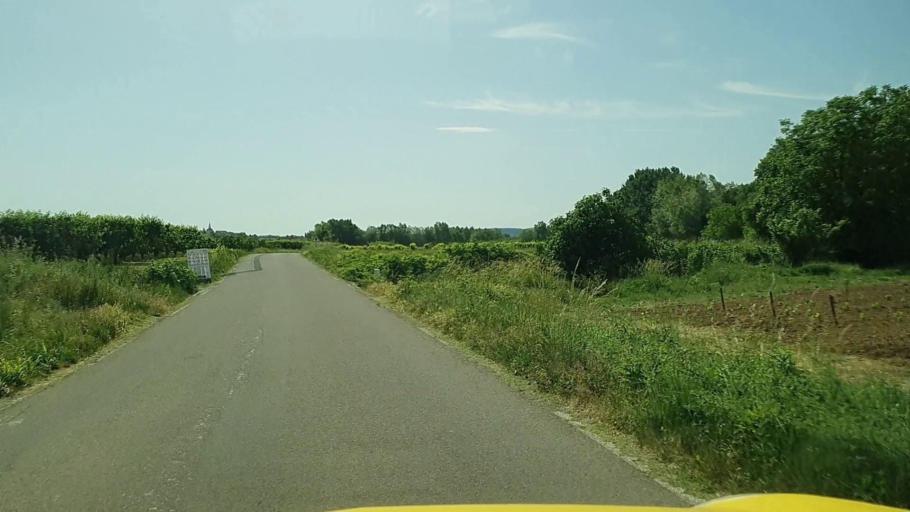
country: FR
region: Languedoc-Roussillon
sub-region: Departement du Gard
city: Sabran
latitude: 44.1055
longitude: 4.5396
